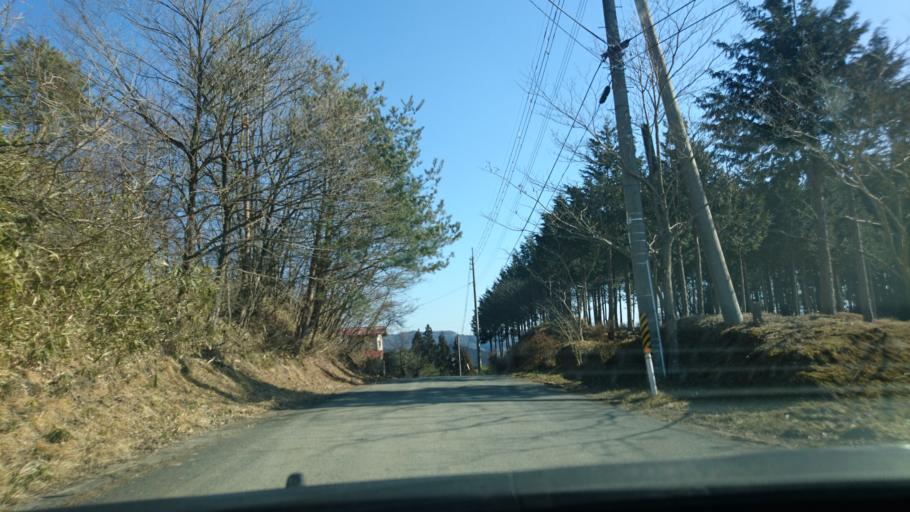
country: JP
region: Iwate
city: Ichinoseki
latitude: 38.8483
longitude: 141.2347
